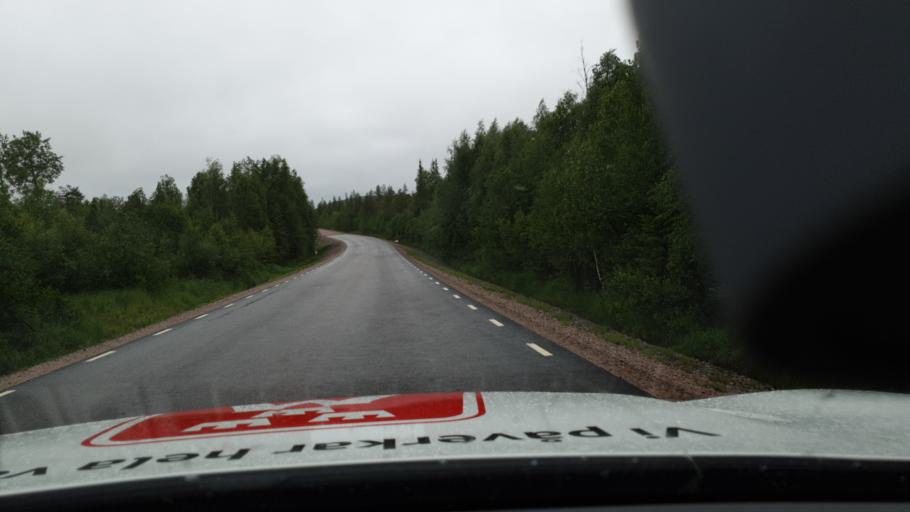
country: SE
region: Norrbotten
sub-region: Overtornea Kommun
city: OEvertornea
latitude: 66.5271
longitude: 23.3708
